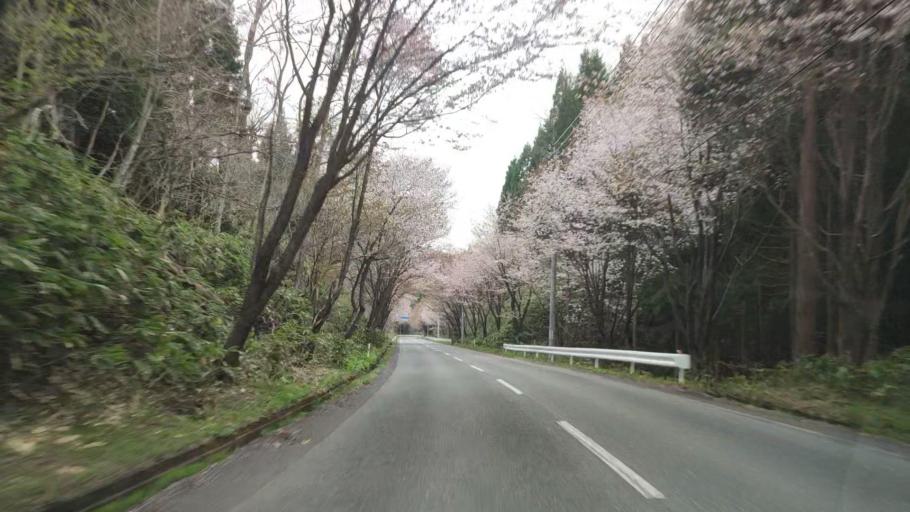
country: JP
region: Akita
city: Hanawa
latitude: 40.3660
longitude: 140.7853
